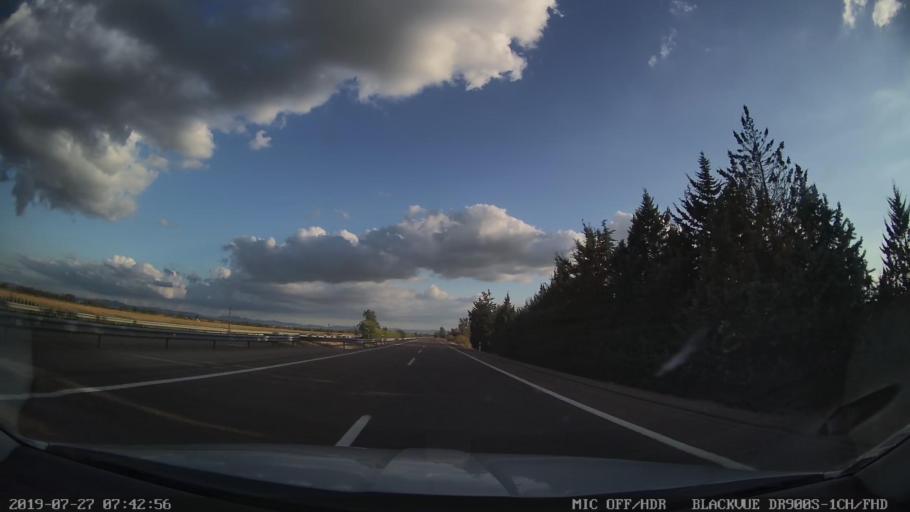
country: ES
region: Extremadura
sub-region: Provincia de Badajoz
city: Santa Amalia
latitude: 39.0051
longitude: -6.0909
